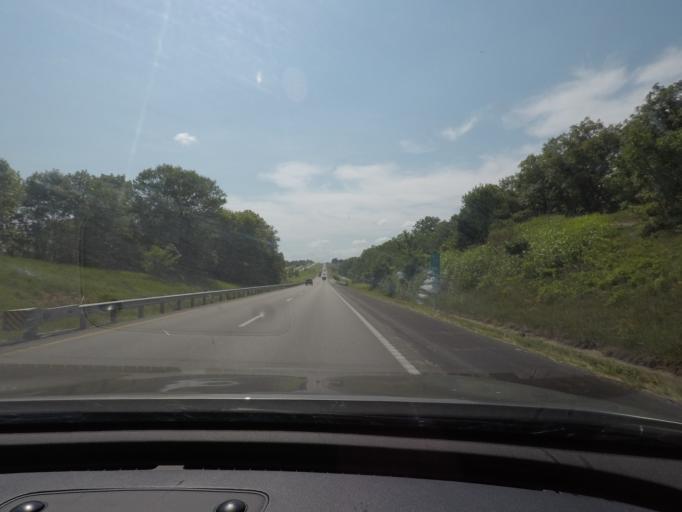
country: US
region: Missouri
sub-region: Lafayette County
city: Odessa
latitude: 39.0105
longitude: -94.0284
